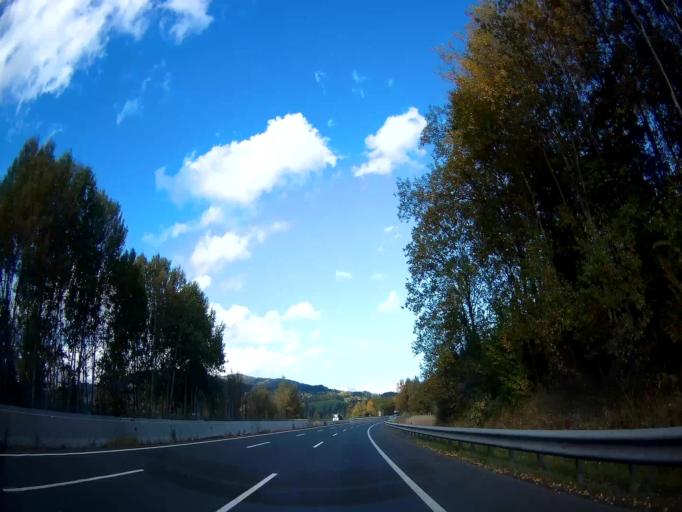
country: AT
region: Carinthia
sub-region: Politischer Bezirk Wolfsberg
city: Bad Sankt Leonhard im Lavanttal
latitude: 46.9318
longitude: 14.8449
